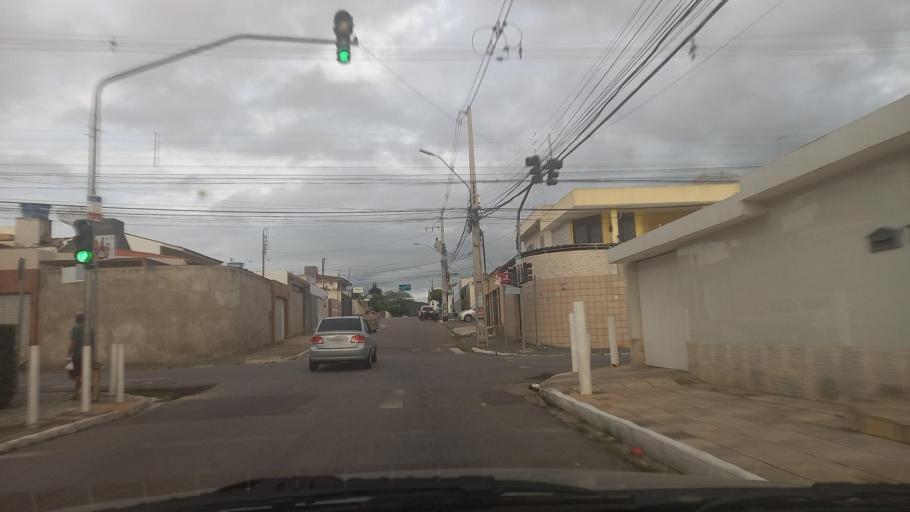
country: BR
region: Pernambuco
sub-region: Caruaru
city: Caruaru
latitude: -8.2712
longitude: -35.9662
